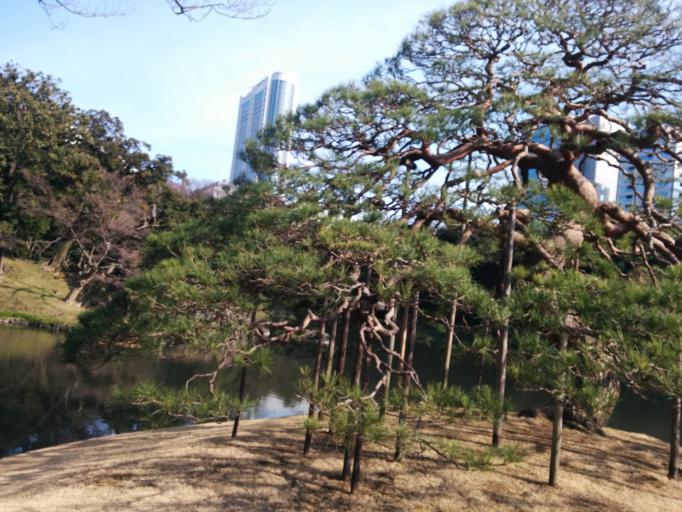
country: JP
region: Tokyo
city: Tokyo
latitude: 35.7054
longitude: 139.7490
